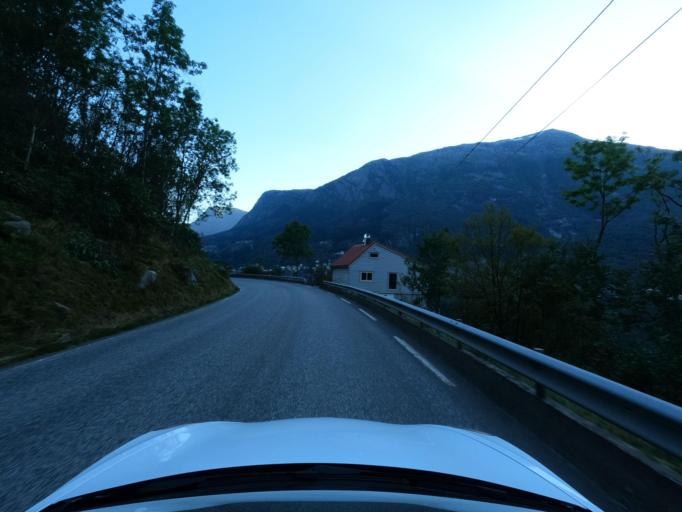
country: NO
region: Hordaland
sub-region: Odda
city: Odda
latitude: 60.0830
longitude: 6.5502
